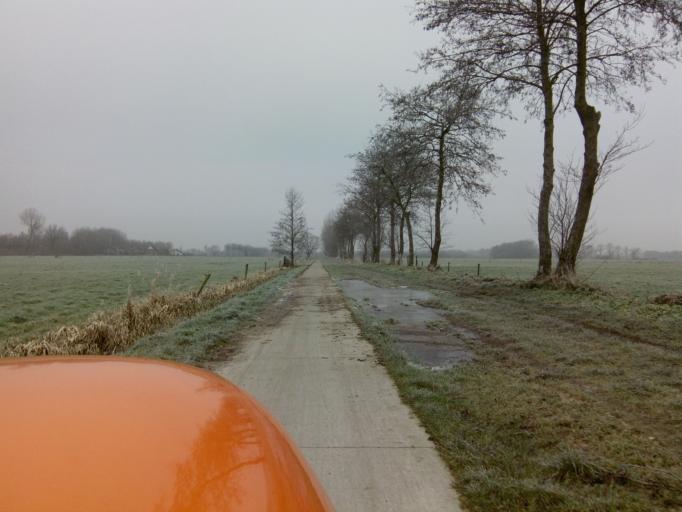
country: NL
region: Gelderland
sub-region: Gemeente Barneveld
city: Terschuur
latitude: 52.1858
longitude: 5.5289
